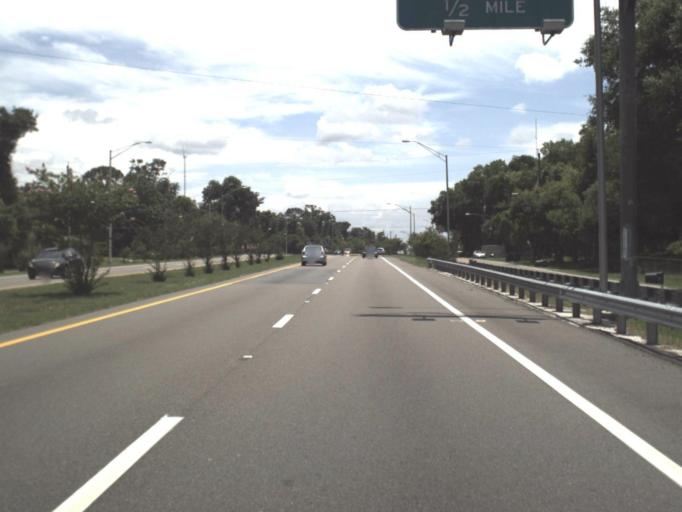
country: US
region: Florida
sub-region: Duval County
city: Jacksonville
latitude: 30.2967
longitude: -81.5587
